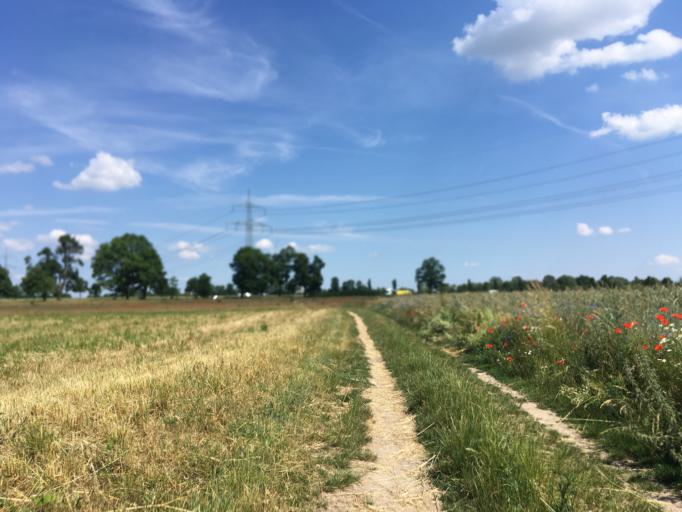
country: DE
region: Brandenburg
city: Neuenhagen
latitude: 52.5475
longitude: 13.6707
